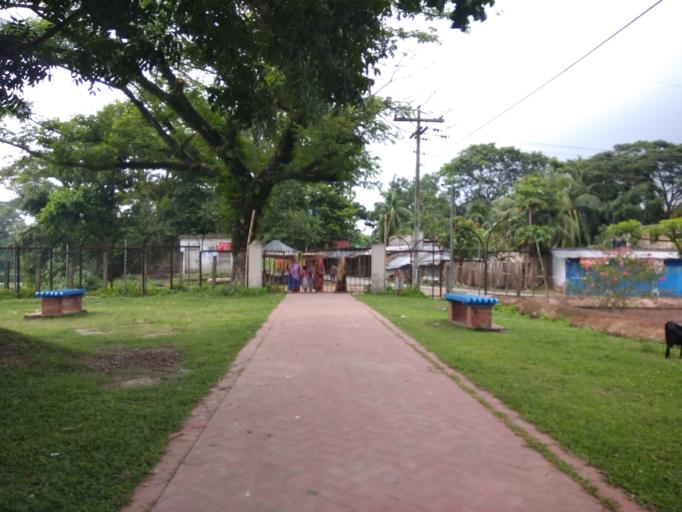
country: BD
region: Khulna
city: Khulna
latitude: 22.6750
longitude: 89.7415
